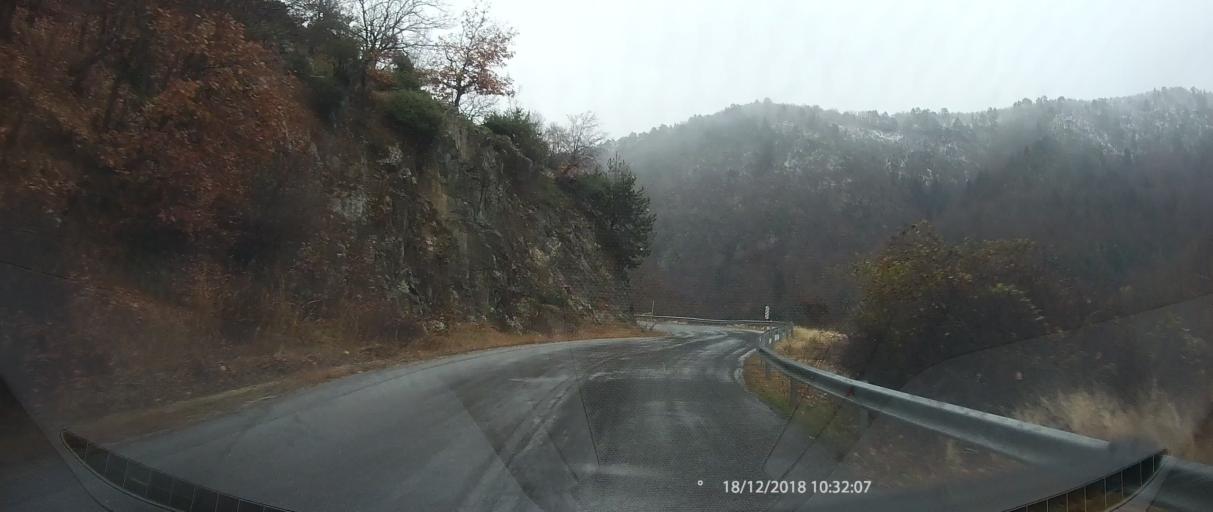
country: GR
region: Central Macedonia
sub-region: Nomos Pierias
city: Kato Milia
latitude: 40.1910
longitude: 22.2891
